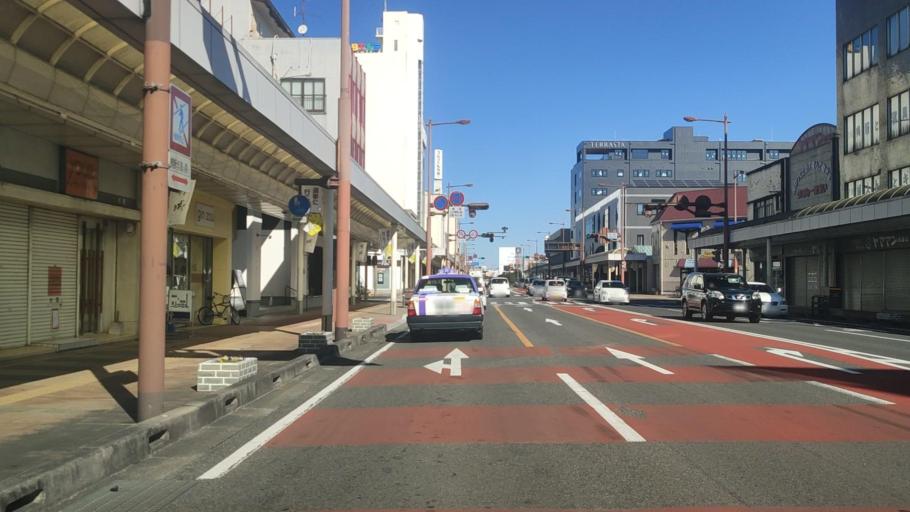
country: JP
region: Miyazaki
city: Miyakonojo
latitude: 31.7248
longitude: 131.0635
